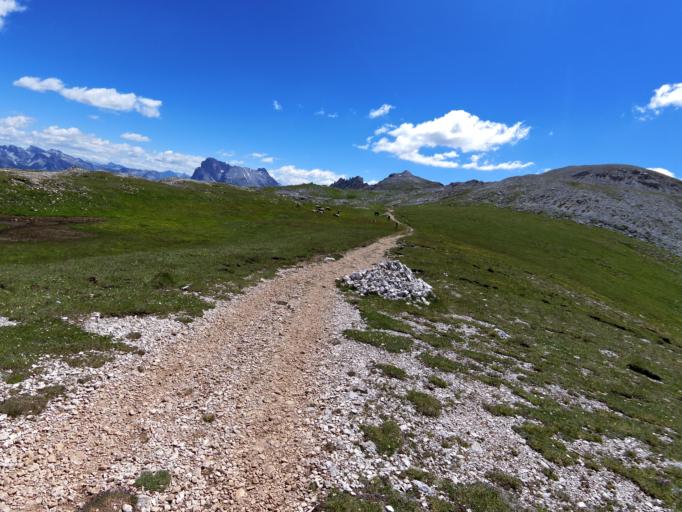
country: IT
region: Trentino-Alto Adige
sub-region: Bolzano
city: Siusi
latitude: 46.5054
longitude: 11.5900
